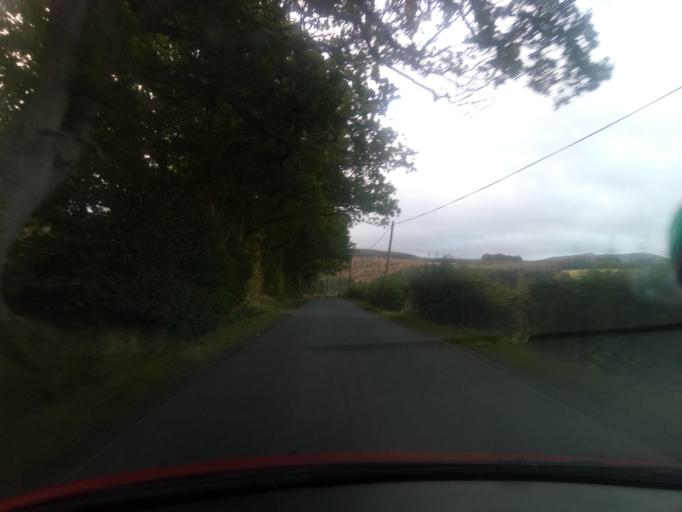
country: GB
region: Scotland
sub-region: The Scottish Borders
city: Hawick
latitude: 55.3684
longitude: -2.6503
